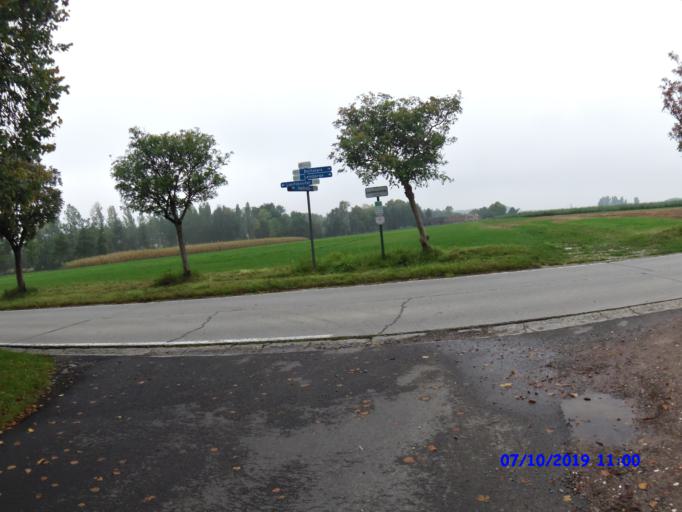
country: BE
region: Flanders
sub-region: Provincie Oost-Vlaanderen
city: Oosterzele
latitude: 50.9734
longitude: 3.7817
